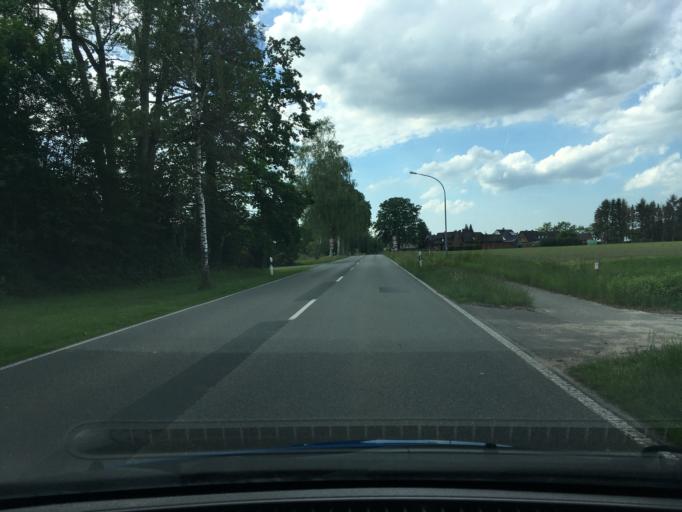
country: DE
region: Lower Saxony
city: Otter
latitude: 53.2585
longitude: 9.7418
